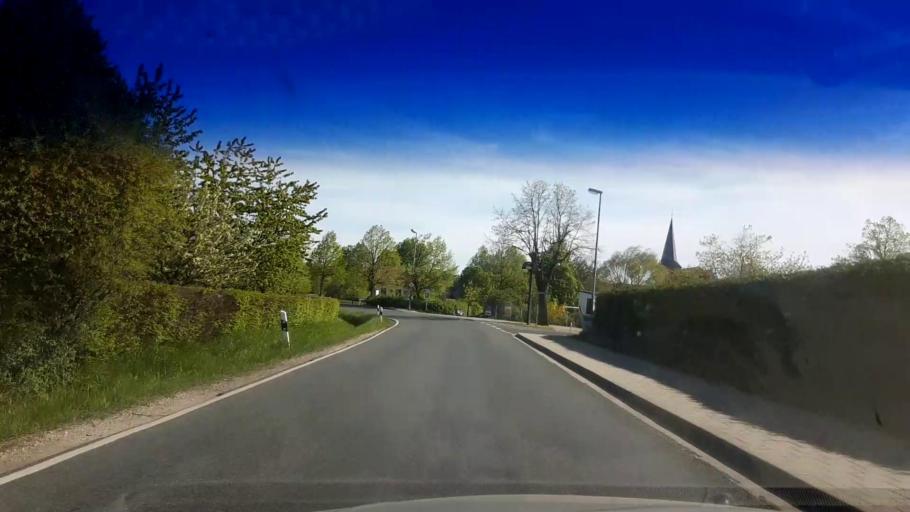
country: DE
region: Bavaria
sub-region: Upper Franconia
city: Buttenheim
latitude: 49.8054
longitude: 11.0311
